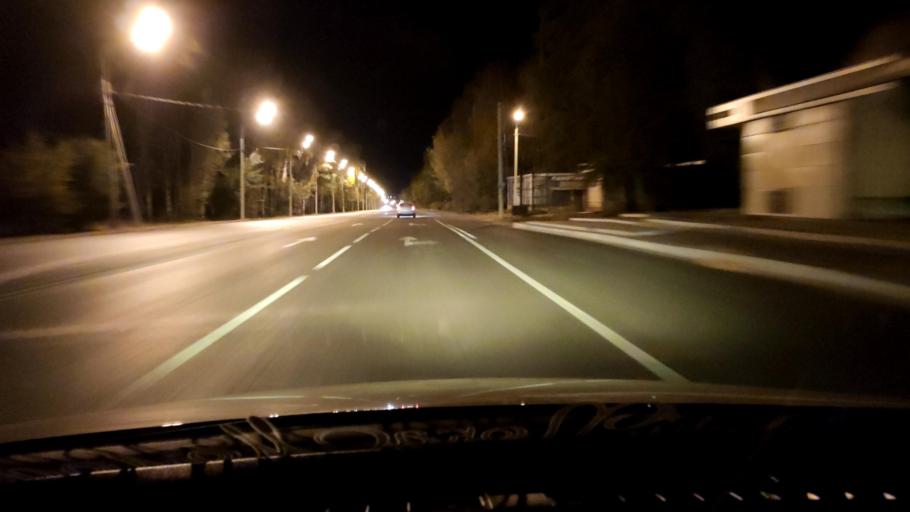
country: RU
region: Voronezj
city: Pridonskoy
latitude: 51.6914
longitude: 39.0986
